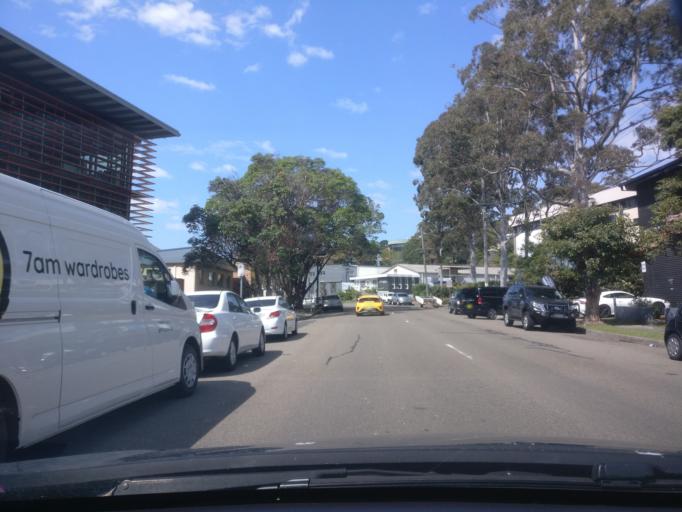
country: AU
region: New South Wales
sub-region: Warringah
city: North Manly
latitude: -33.7667
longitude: 151.2620
